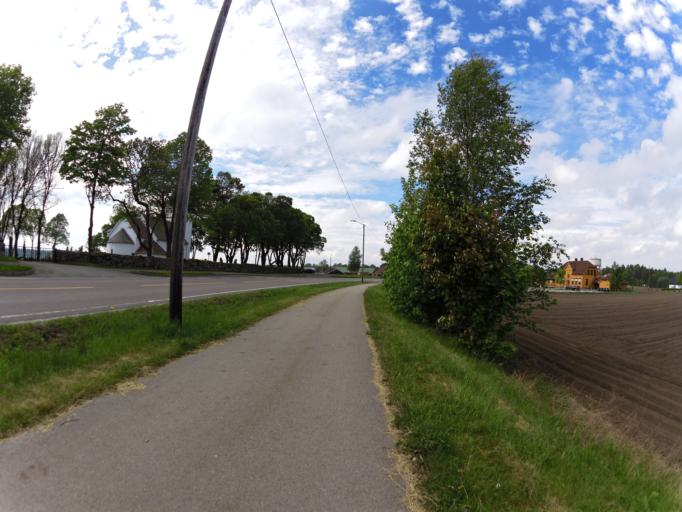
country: NO
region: Ostfold
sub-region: Rade
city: Karlshus
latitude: 59.3464
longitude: 10.8955
